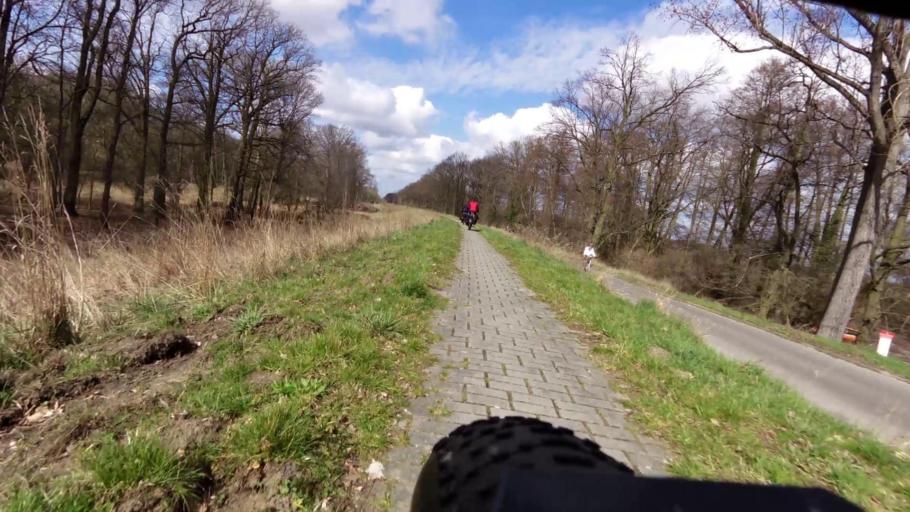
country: PL
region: Lubusz
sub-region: Powiat slubicki
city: Slubice
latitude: 52.3711
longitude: 14.5625
